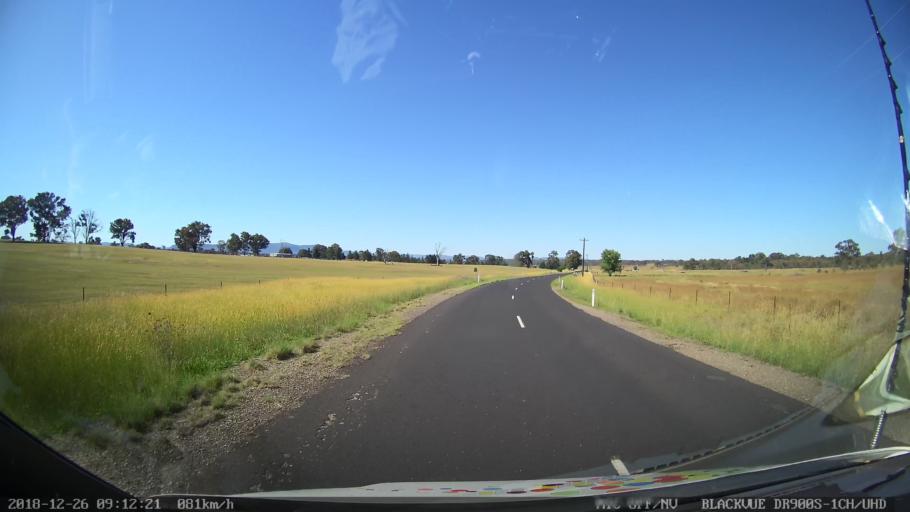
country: AU
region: New South Wales
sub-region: Mid-Western Regional
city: Kandos
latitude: -32.7570
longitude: 149.9830
